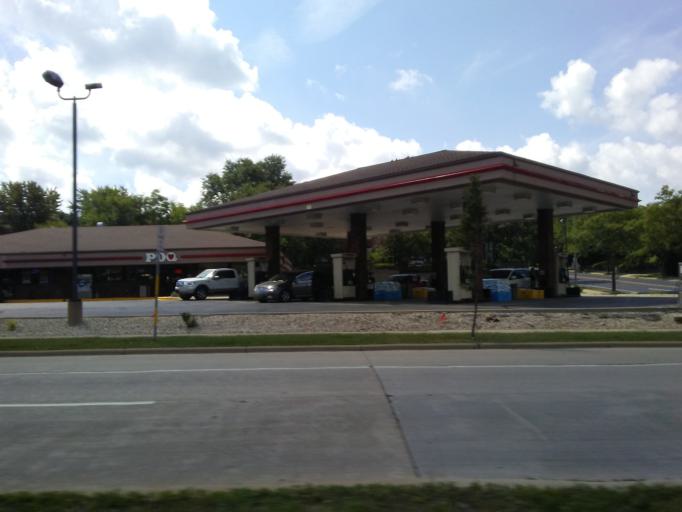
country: US
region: Wisconsin
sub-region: Dane County
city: Middleton
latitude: 43.0605
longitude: -89.5171
